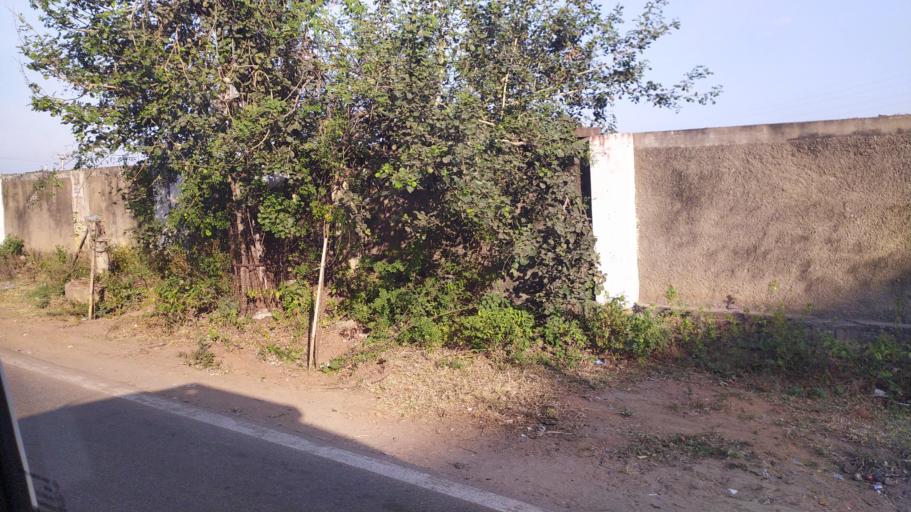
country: IN
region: Telangana
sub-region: Hyderabad
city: Hyderabad
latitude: 17.3272
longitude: 78.4205
